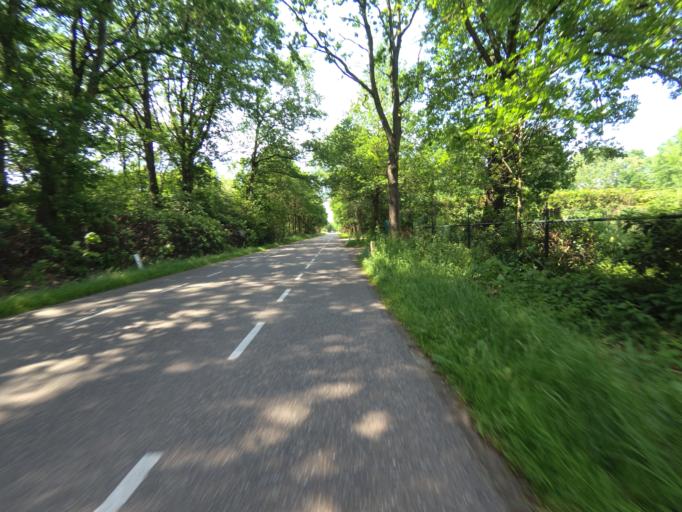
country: NL
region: Gelderland
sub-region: Gemeente Ede
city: Ede
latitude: 52.0781
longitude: 5.6724
